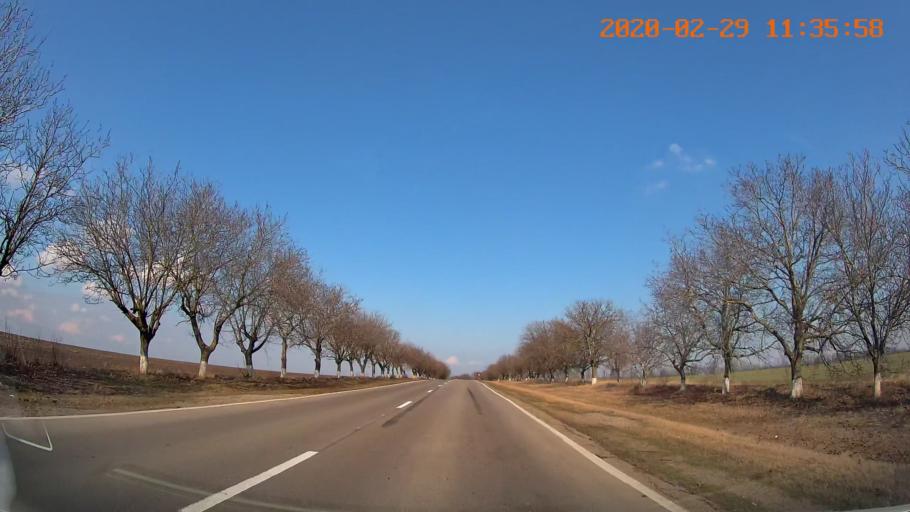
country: MD
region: Rezina
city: Saharna
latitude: 47.5888
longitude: 29.0597
